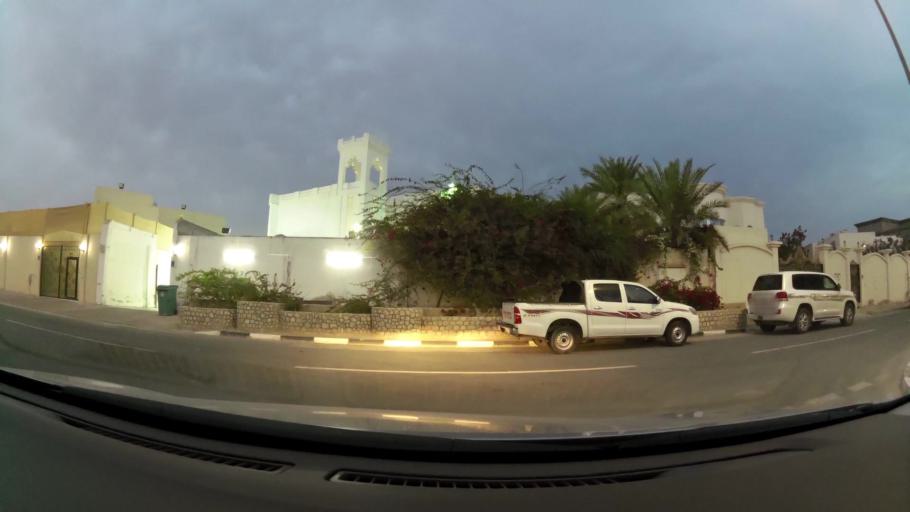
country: QA
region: Baladiyat ad Dawhah
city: Doha
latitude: 25.3433
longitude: 51.5104
